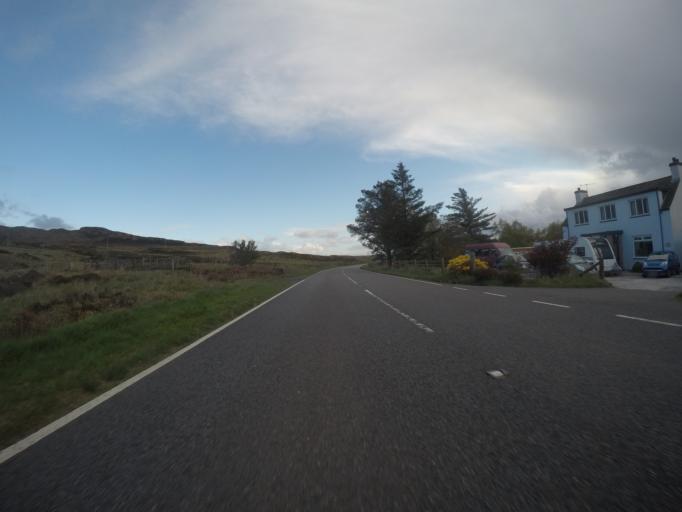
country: GB
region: Scotland
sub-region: Highland
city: Portree
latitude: 57.5596
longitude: -6.3633
